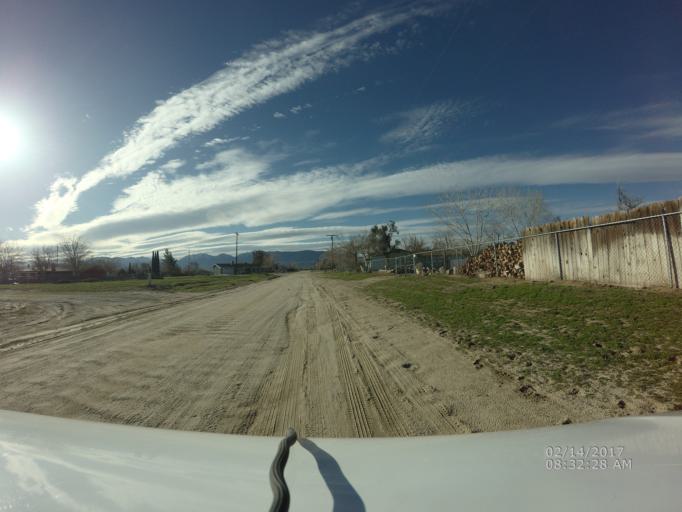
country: US
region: California
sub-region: Los Angeles County
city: Littlerock
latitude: 34.5455
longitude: -117.9450
